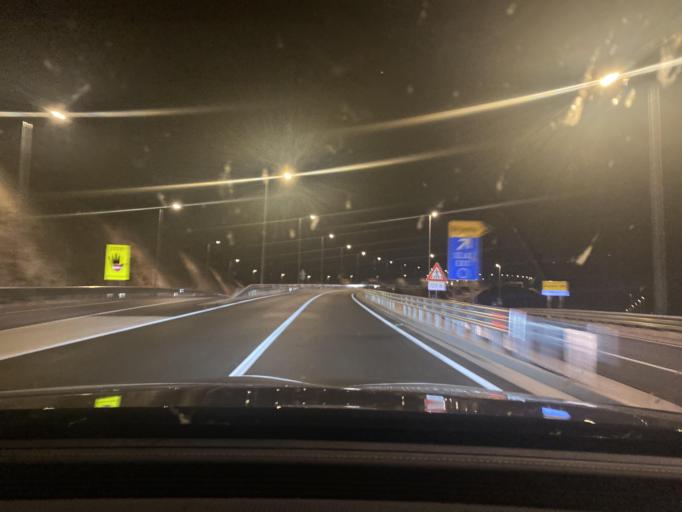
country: BA
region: Federation of Bosnia and Herzegovina
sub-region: Hercegovacko-Bosanski Kanton
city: Neum
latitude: 42.9082
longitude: 17.5349
